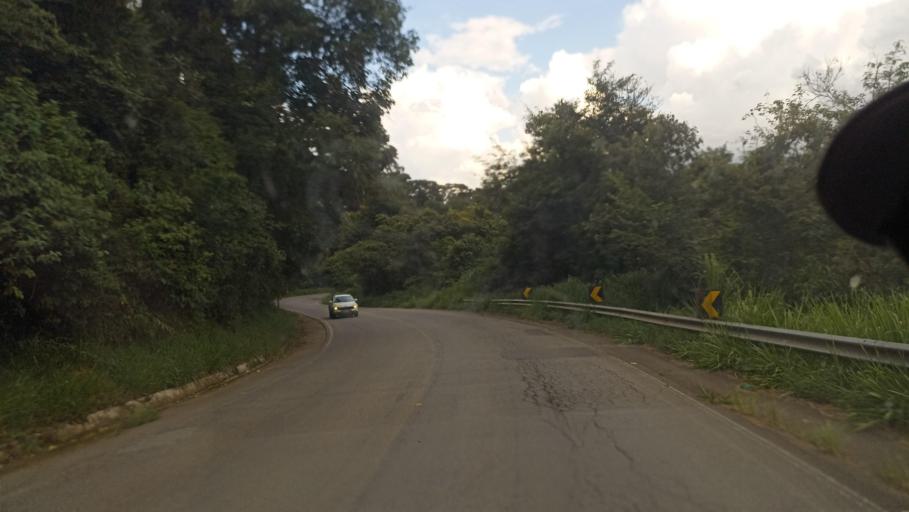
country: BR
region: Minas Gerais
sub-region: Cruzilia
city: Cruzilia
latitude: -21.8773
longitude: -44.8135
